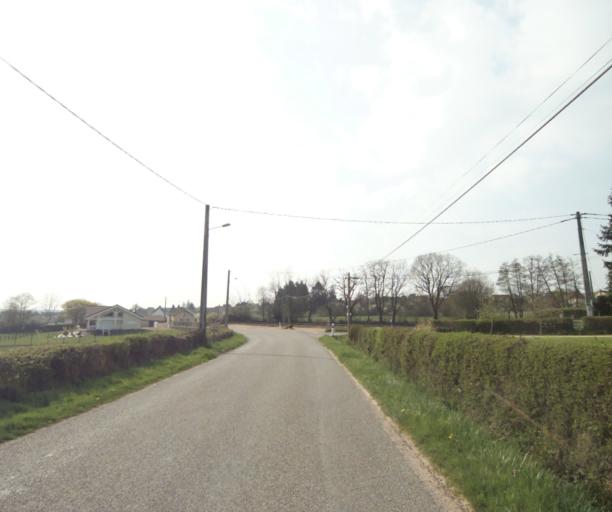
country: FR
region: Bourgogne
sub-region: Departement de Saone-et-Loire
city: Charolles
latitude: 46.4835
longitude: 4.4452
